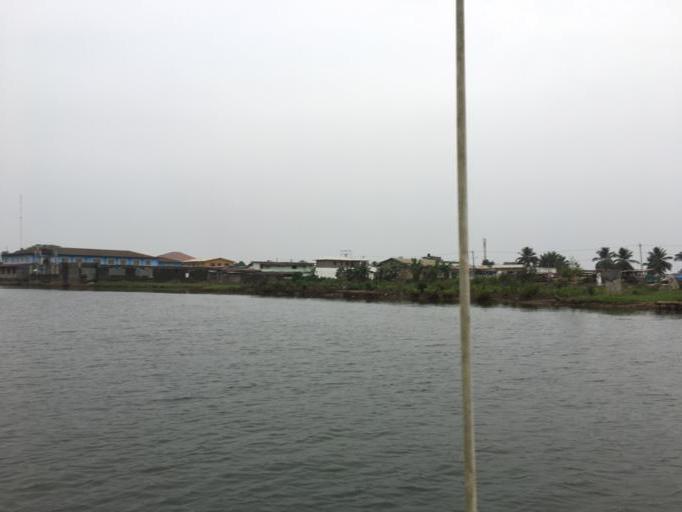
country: LR
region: Montserrado
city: Monrovia
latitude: 6.3836
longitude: -10.7803
